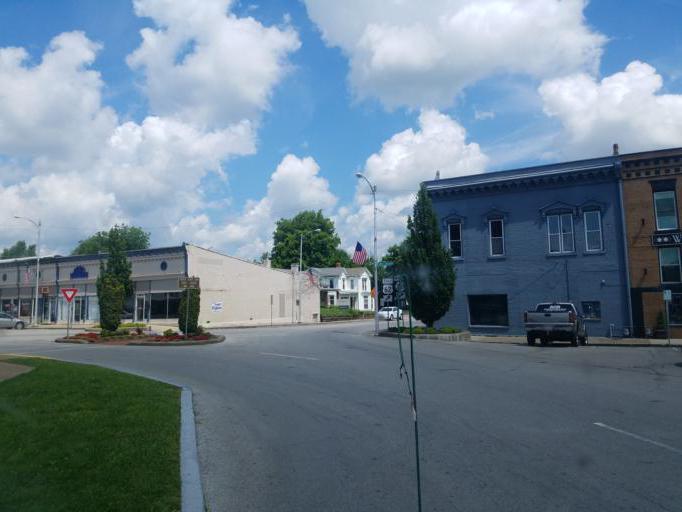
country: US
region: Kentucky
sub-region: Grayson County
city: Leitchfield
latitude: 37.4802
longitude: -86.2935
